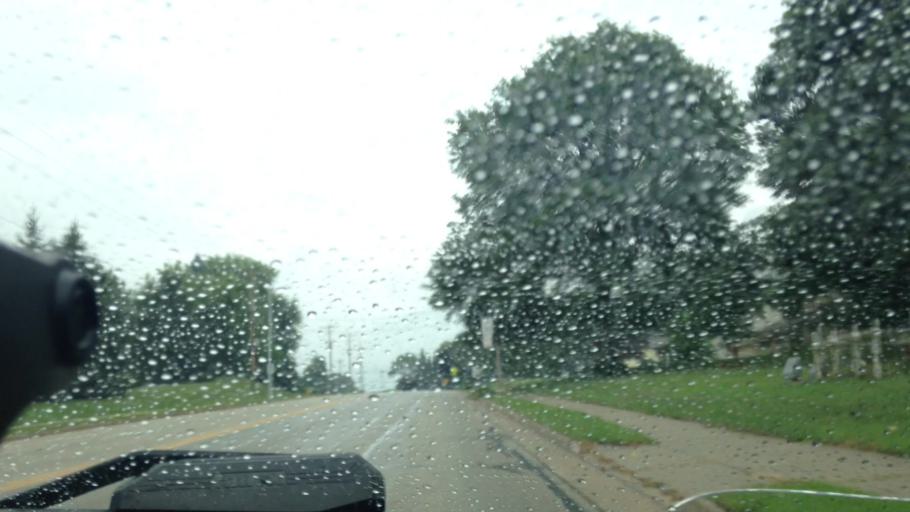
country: US
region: Wisconsin
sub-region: Washington County
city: Slinger
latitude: 43.3281
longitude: -88.2755
